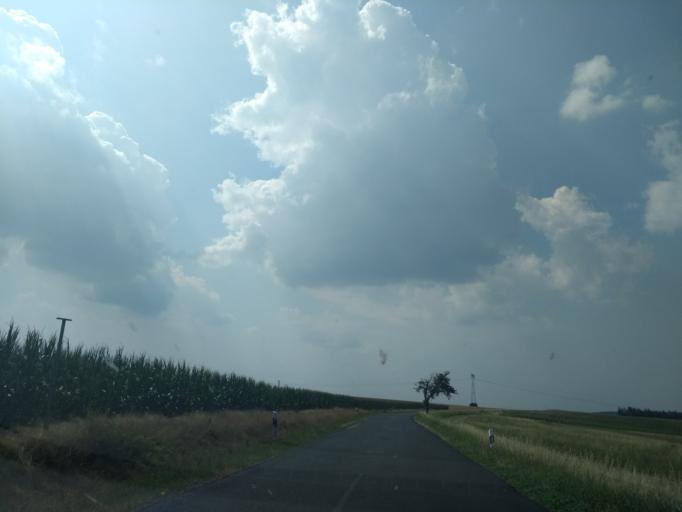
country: DE
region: Thuringia
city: Eisenberg
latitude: 50.9817
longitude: 11.9260
